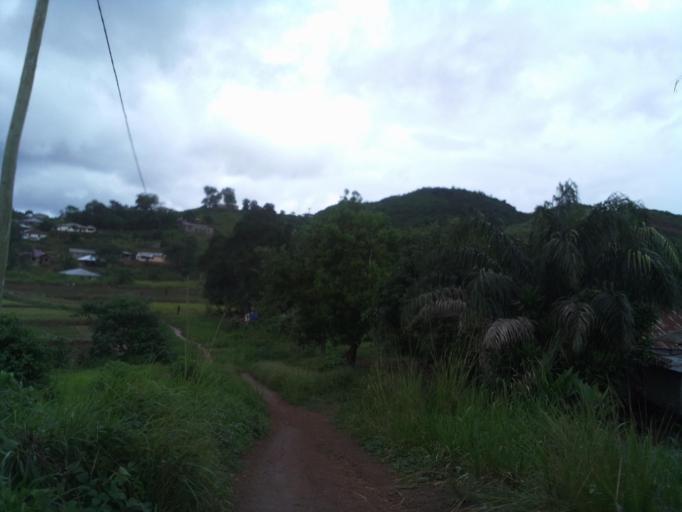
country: SL
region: Eastern Province
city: Kenema
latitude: 7.8469
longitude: -11.1861
